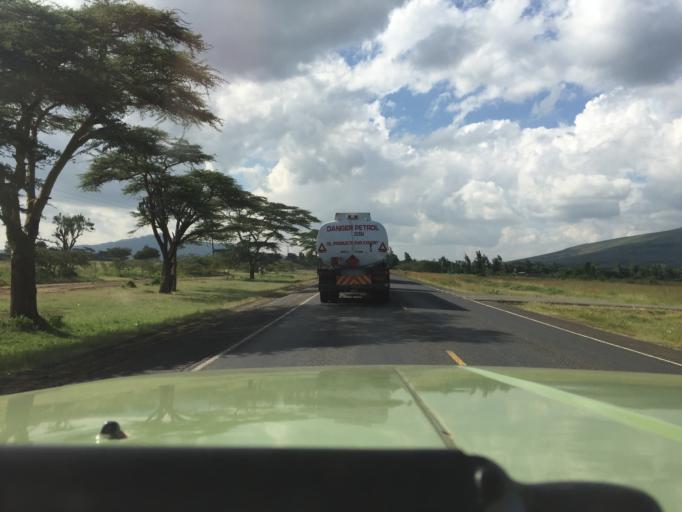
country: KE
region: Nakuru
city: Kijabe
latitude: -0.9607
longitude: 36.5598
